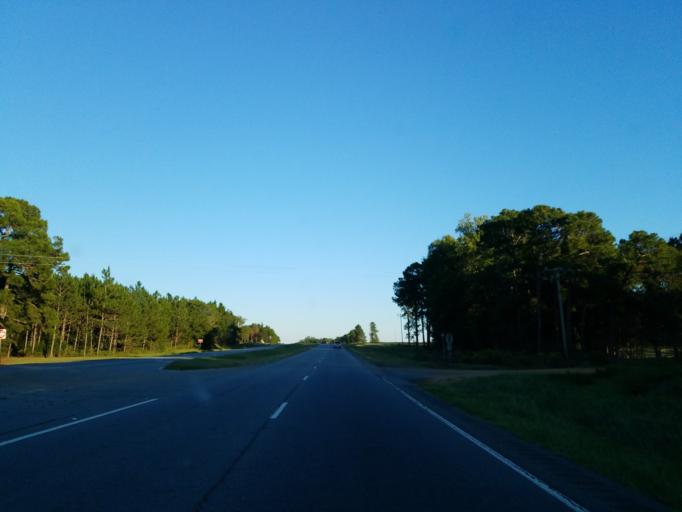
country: US
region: Georgia
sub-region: Worth County
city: Sylvester
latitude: 31.4845
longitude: -83.6967
